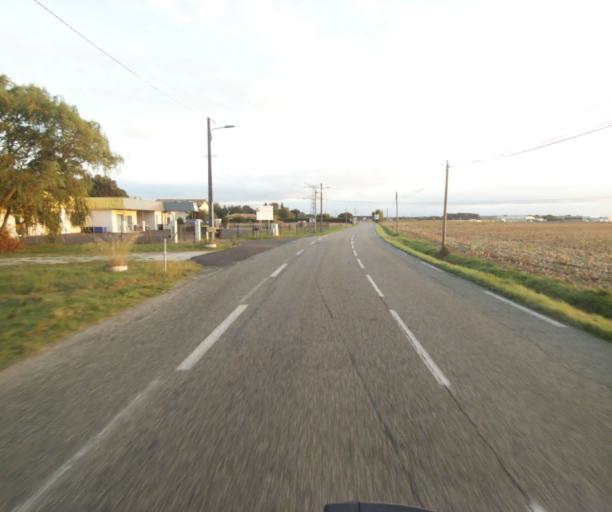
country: FR
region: Midi-Pyrenees
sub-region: Departement du Tarn-et-Garonne
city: Verdun-sur-Garonne
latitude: 43.8267
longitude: 1.2439
